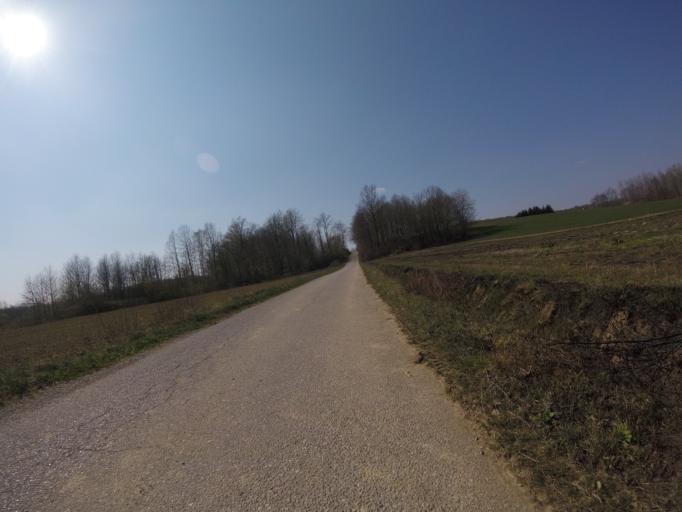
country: HR
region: Grad Zagreb
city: Strmec
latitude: 45.5583
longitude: 15.9169
